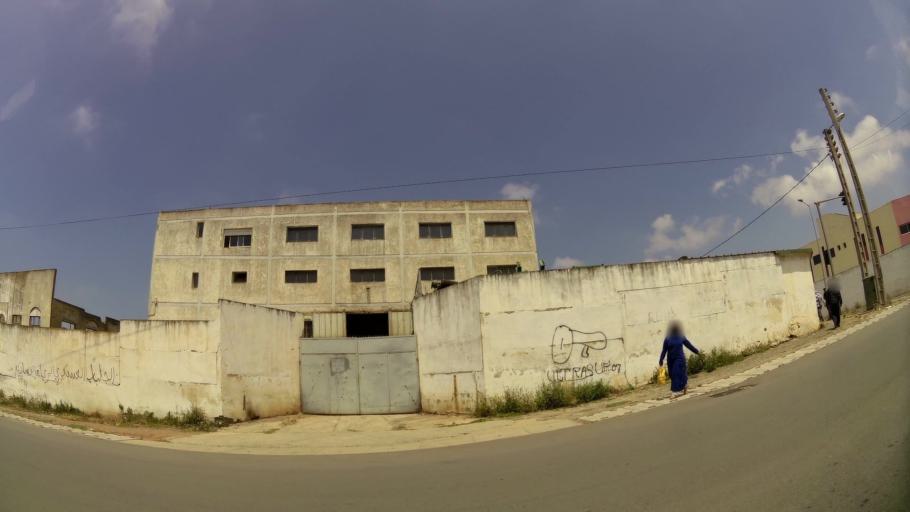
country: MA
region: Rabat-Sale-Zemmour-Zaer
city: Sale
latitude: 34.0604
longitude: -6.7918
